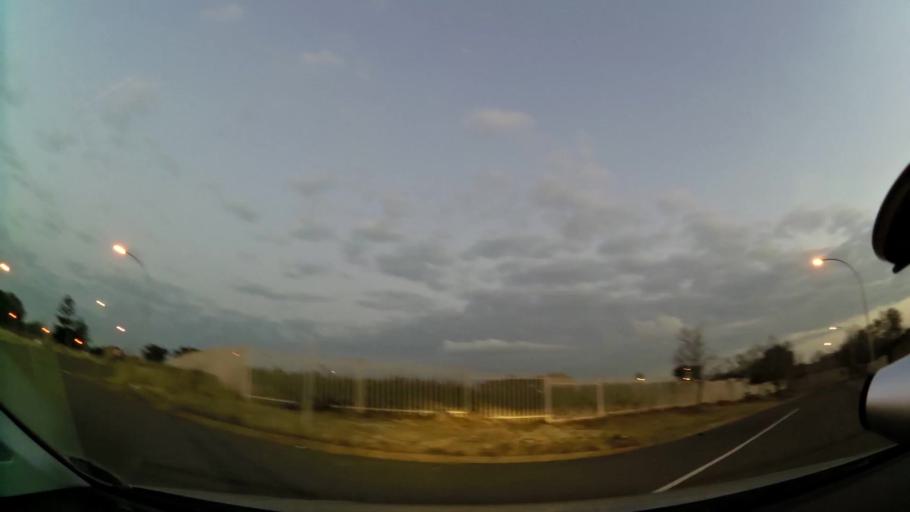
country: ZA
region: Orange Free State
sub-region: Mangaung Metropolitan Municipality
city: Bloemfontein
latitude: -29.1510
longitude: 26.1931
